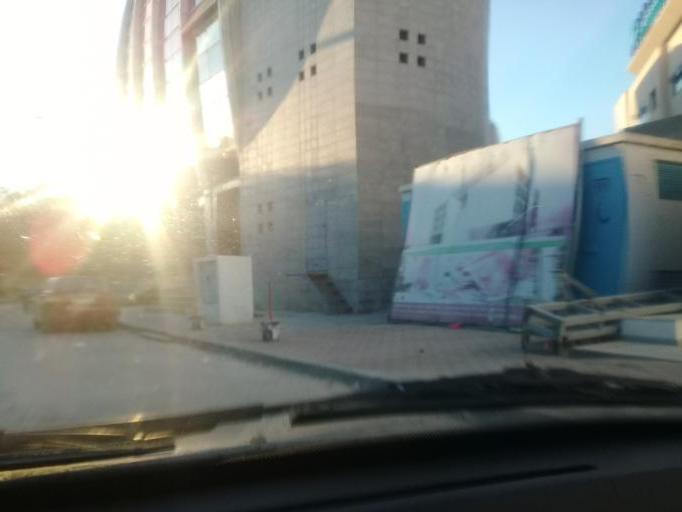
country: TN
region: Tunis
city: La Goulette
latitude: 36.8469
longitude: 10.2654
